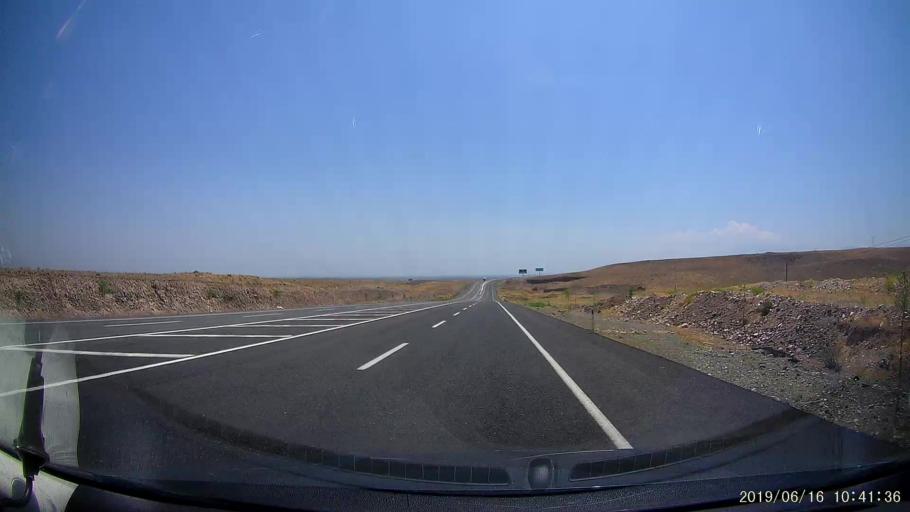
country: TR
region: Igdir
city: Tuzluca
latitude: 40.0470
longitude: 43.7869
